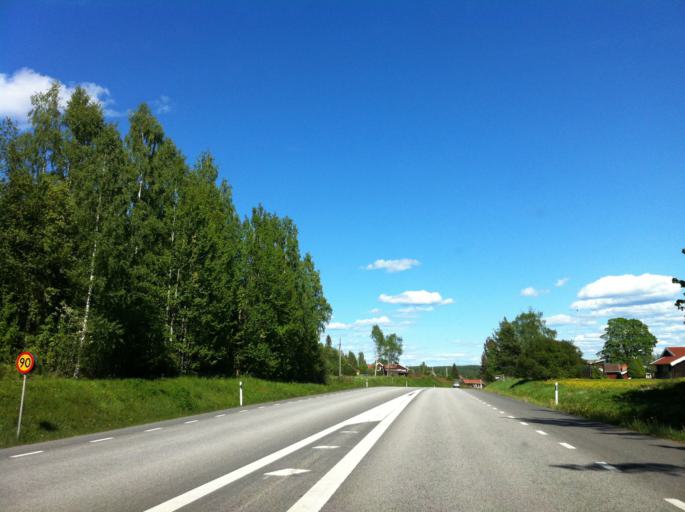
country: SE
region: Dalarna
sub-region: Rattviks Kommun
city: Vikarbyn
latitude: 60.9111
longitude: 15.0151
